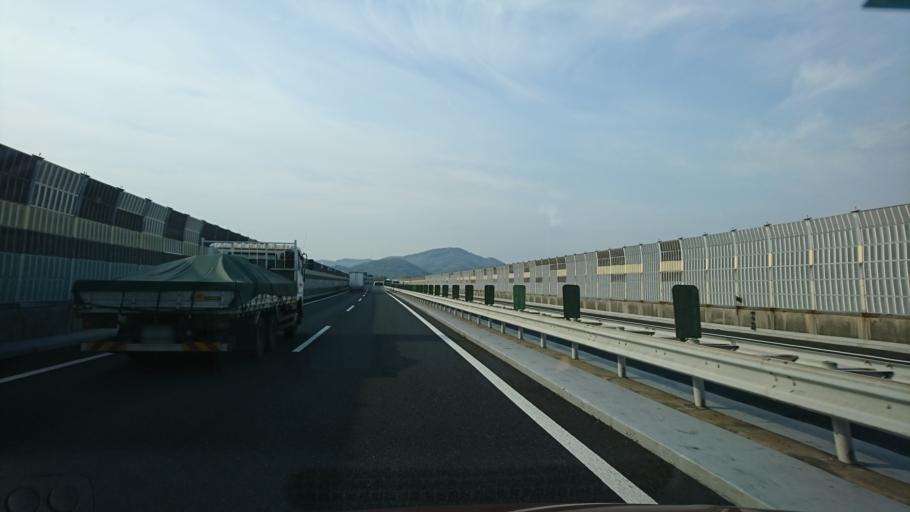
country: JP
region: Okayama
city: Okayama-shi
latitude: 34.7495
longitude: 134.0327
